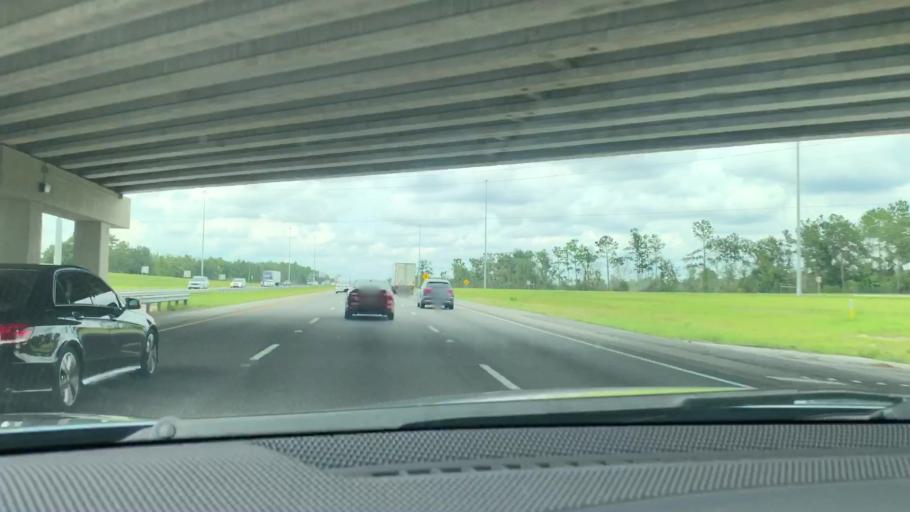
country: US
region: Georgia
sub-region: McIntosh County
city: Darien
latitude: 31.3963
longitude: -81.4485
